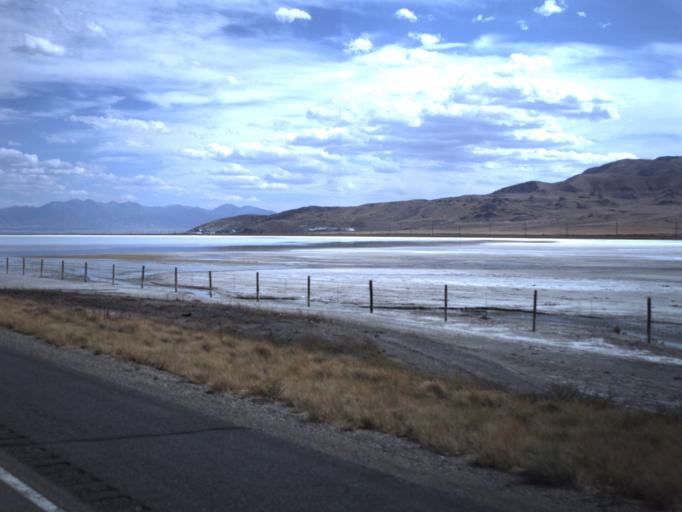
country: US
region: Utah
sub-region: Tooele County
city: Grantsville
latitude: 40.7373
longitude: -112.6146
